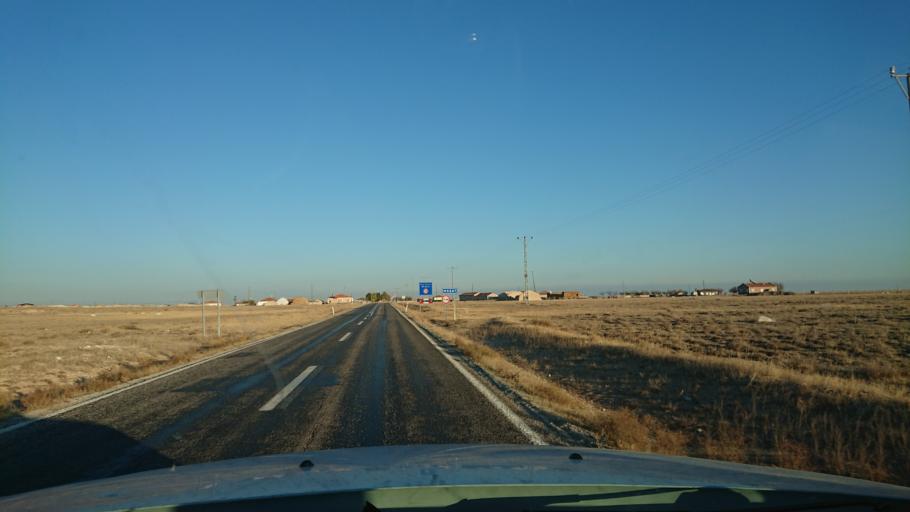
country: TR
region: Aksaray
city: Eskil
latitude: 38.4641
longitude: 33.2428
